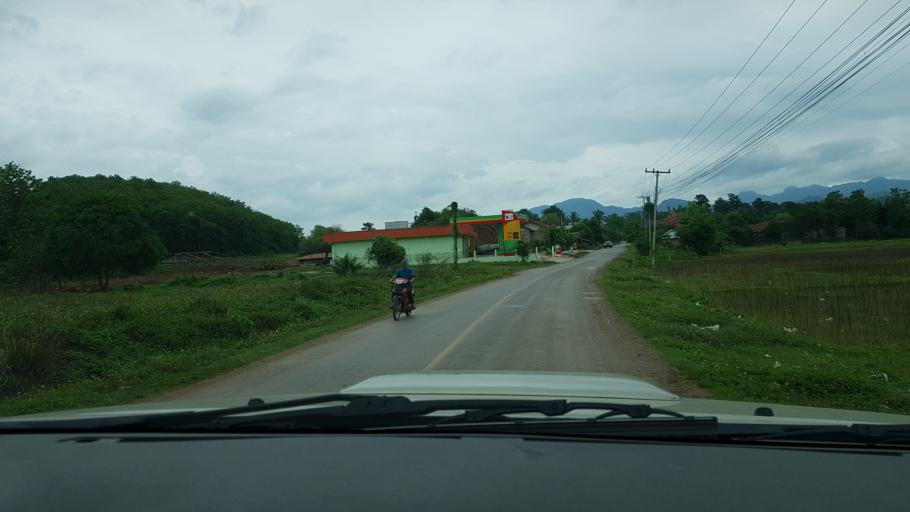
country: LA
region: Loungnamtha
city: Muang Nale
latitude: 20.2896
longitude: 101.6314
